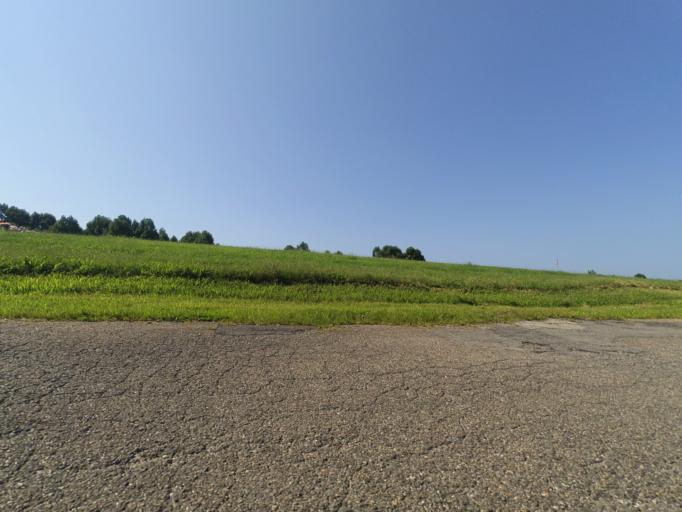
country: US
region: West Virginia
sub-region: Cabell County
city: Huntington
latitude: 38.4375
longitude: -82.4420
